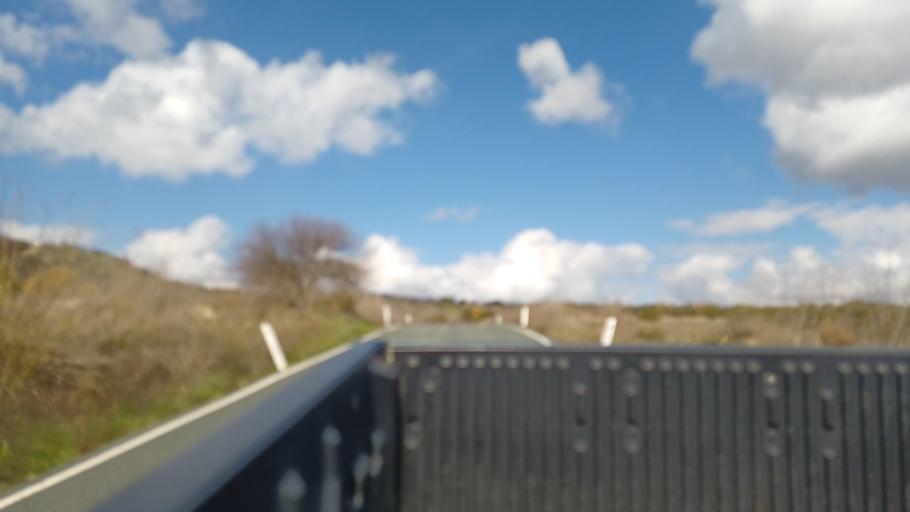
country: CY
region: Limassol
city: Pachna
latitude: 34.7758
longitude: 32.7469
